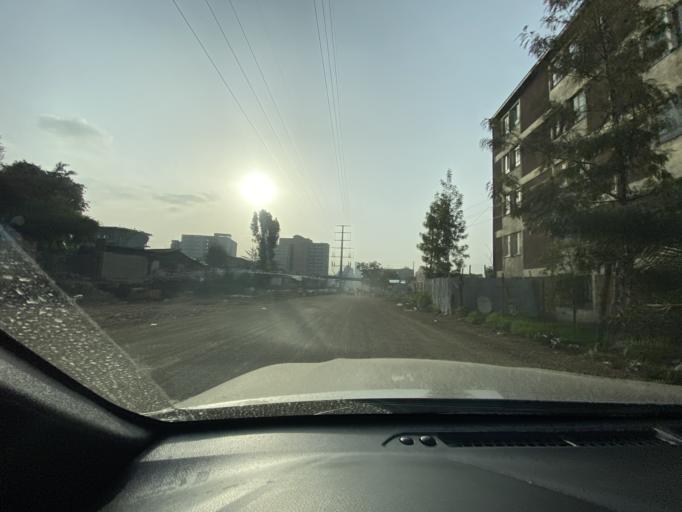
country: ET
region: Adis Abeba
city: Addis Ababa
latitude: 9.0164
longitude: 38.7331
